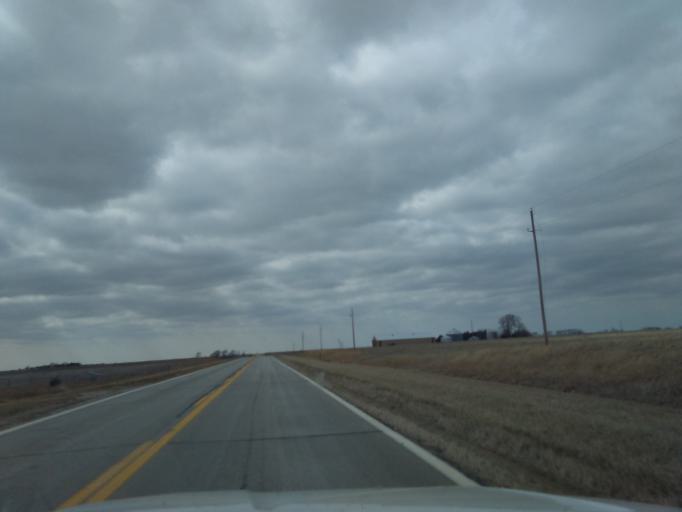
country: US
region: Nebraska
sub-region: Gage County
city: Wymore
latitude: 40.0447
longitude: -96.4416
